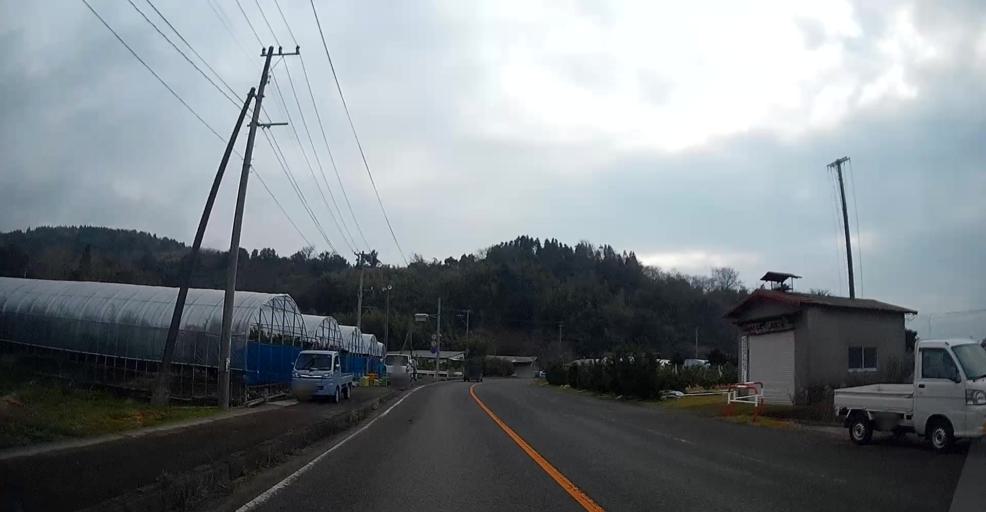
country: JP
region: Kumamoto
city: Matsubase
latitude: 32.6272
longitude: 130.5435
